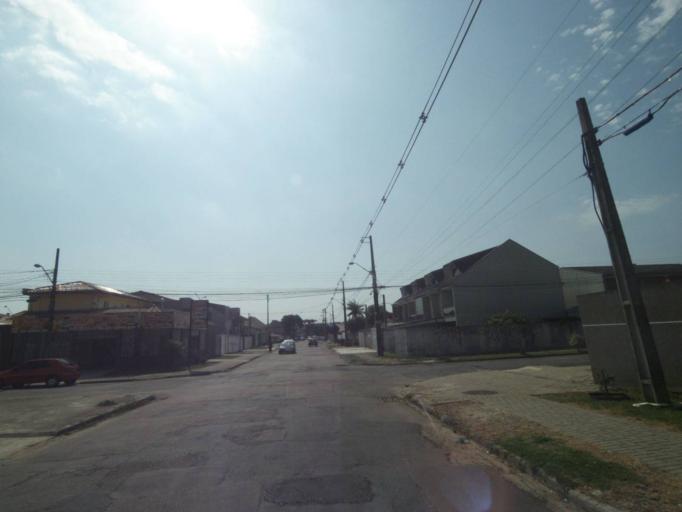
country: BR
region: Parana
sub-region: Curitiba
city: Curitiba
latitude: -25.4877
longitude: -49.3330
